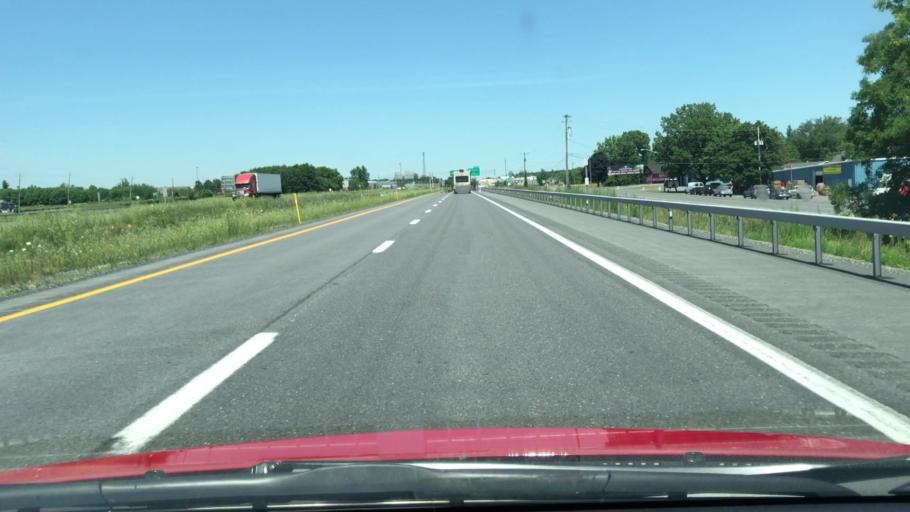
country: US
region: New York
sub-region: Clinton County
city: Champlain
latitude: 44.9930
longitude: -73.4562
